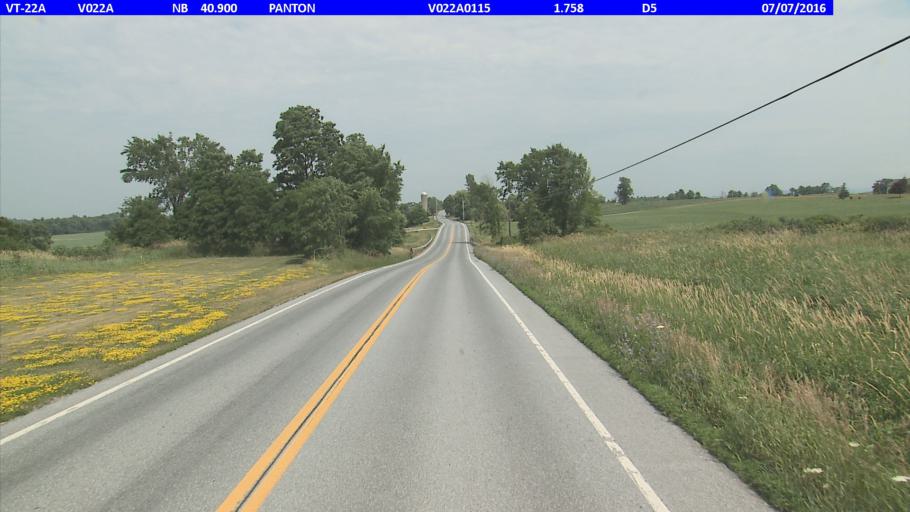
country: US
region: Vermont
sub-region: Addison County
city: Vergennes
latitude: 44.1424
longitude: -73.2784
